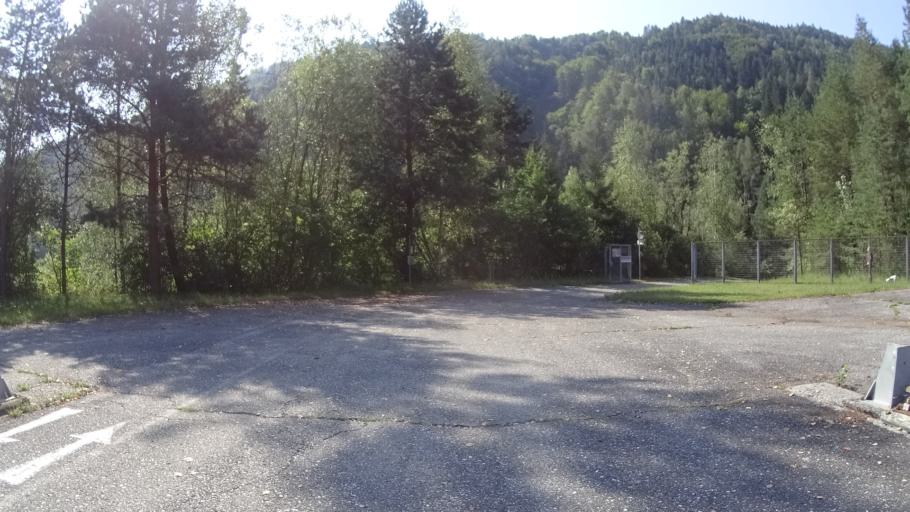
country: AT
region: Carinthia
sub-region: Politischer Bezirk Volkermarkt
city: Gallizien
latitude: 46.5601
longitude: 14.4798
